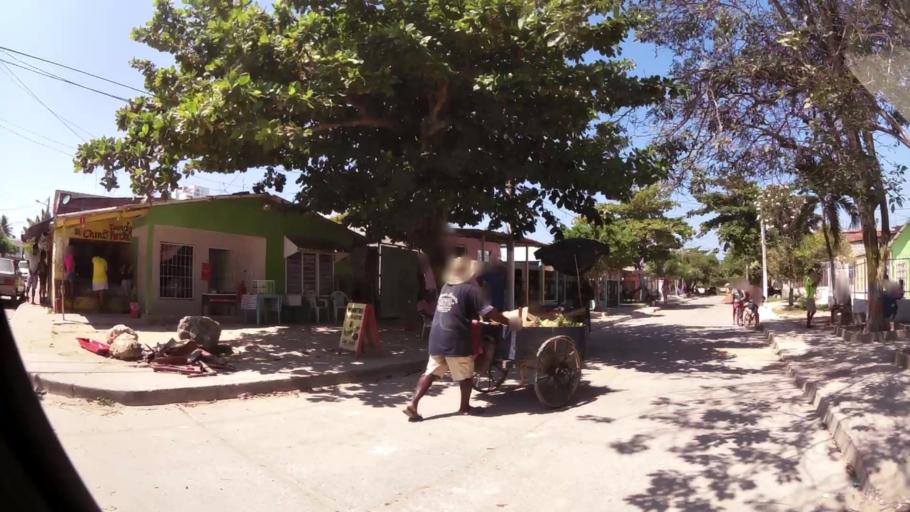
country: CO
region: Bolivar
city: Cartagena
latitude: 10.4355
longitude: -75.5318
